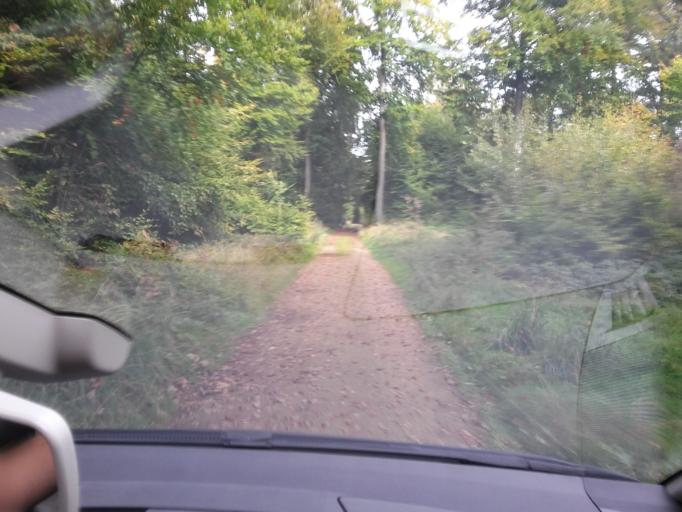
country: BE
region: Wallonia
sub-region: Province du Luxembourg
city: Attert
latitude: 49.7199
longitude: 5.7764
